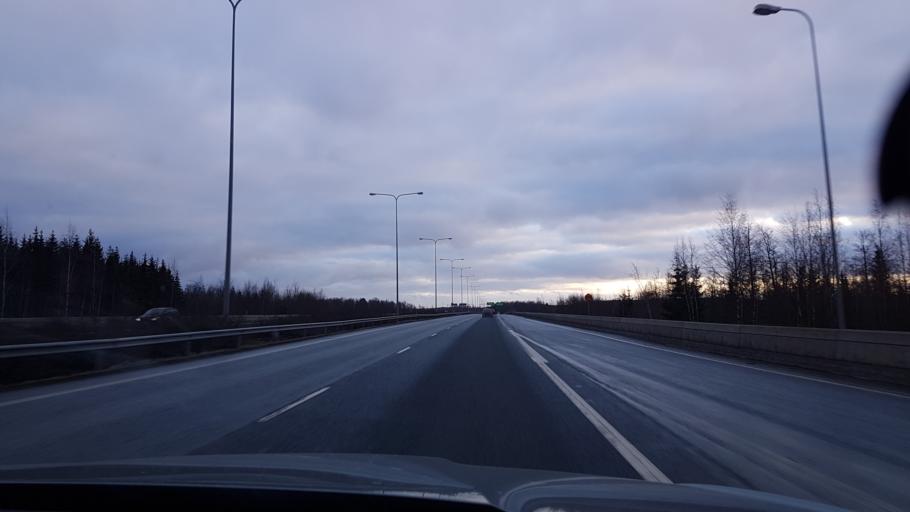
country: FI
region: Pirkanmaa
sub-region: Etelae-Pirkanmaa
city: Toijala
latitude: 61.2172
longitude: 23.8394
